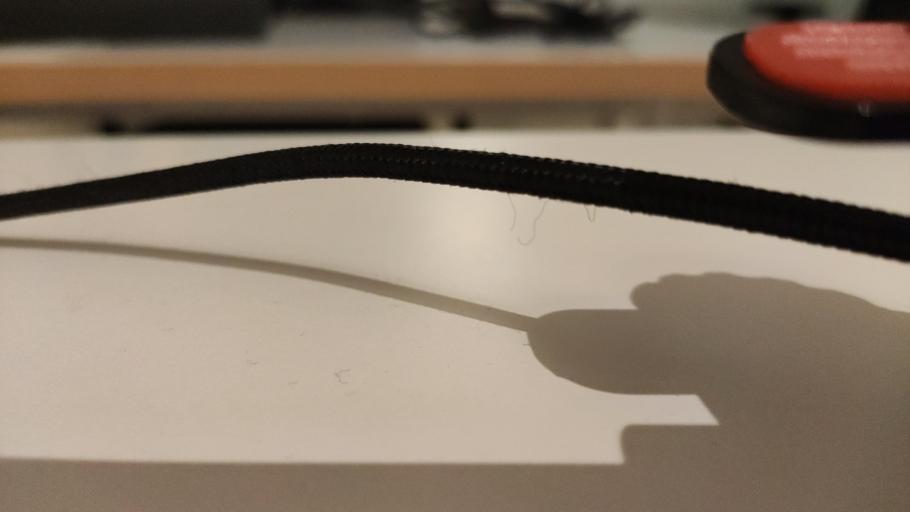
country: RU
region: Moskovskaya
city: Novoye
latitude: 55.6362
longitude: 38.9290
